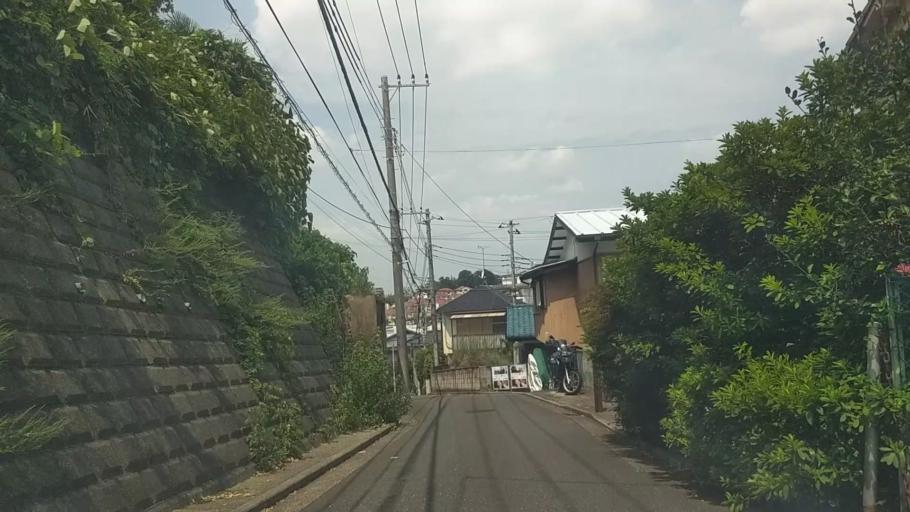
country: JP
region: Kanagawa
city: Yokohama
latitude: 35.5073
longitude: 139.6259
